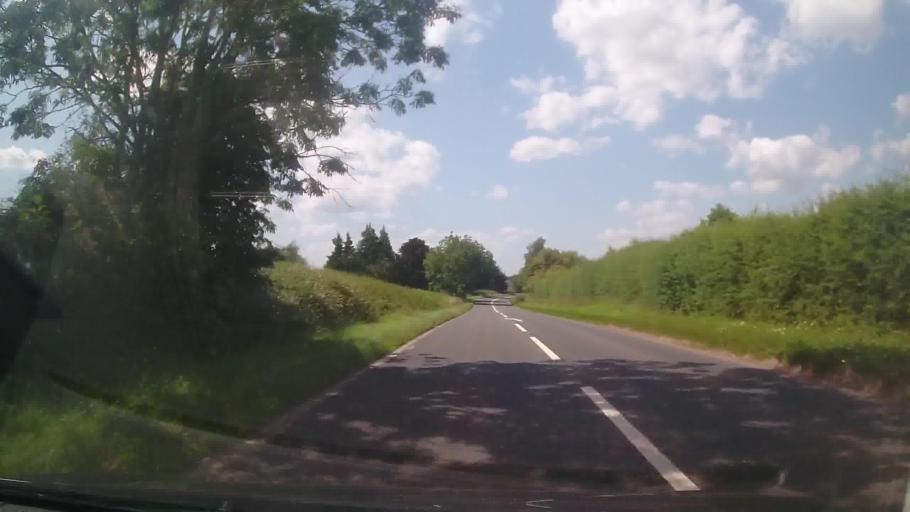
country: GB
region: England
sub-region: Herefordshire
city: Bodenham
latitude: 52.1482
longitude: -2.6416
